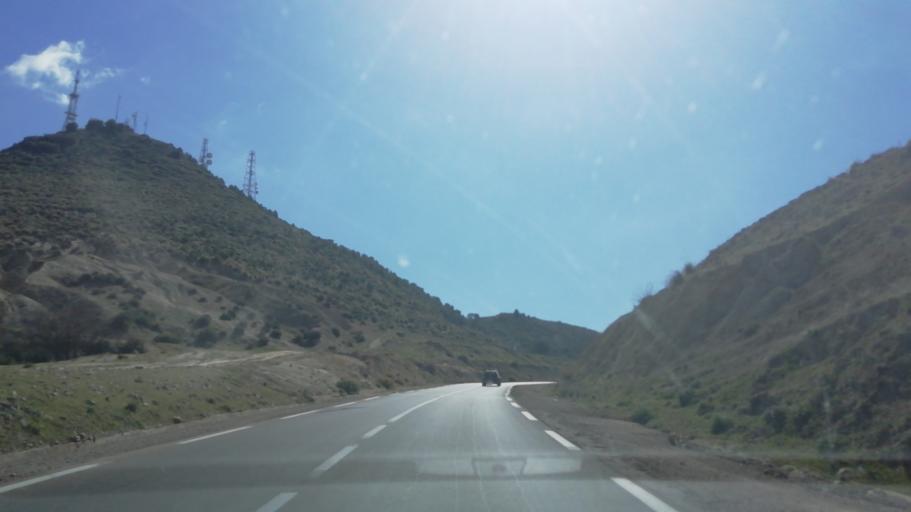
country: DZ
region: Mascara
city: Mascara
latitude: 35.4778
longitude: 0.1588
